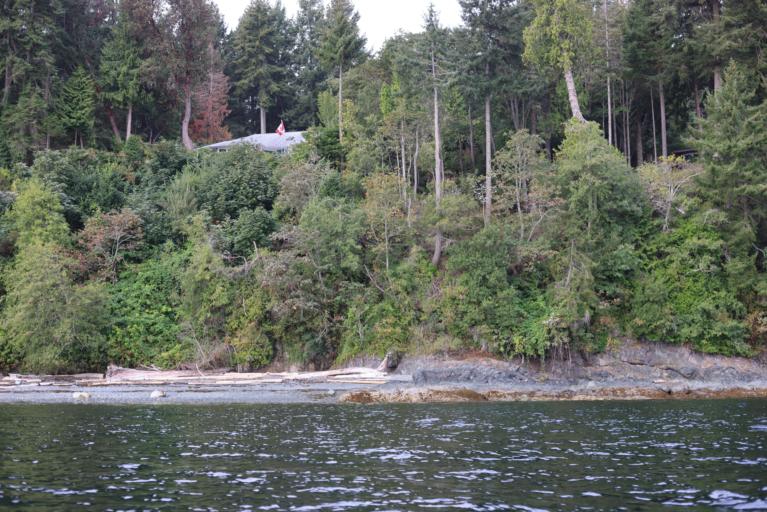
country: CA
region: British Columbia
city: Nanaimo
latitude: 49.2175
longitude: -123.9415
